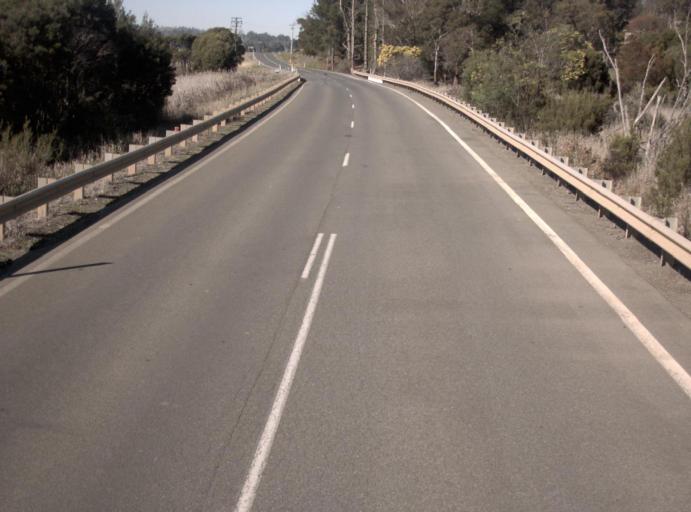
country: AU
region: Tasmania
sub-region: Launceston
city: Mayfield
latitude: -41.3167
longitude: 147.0553
